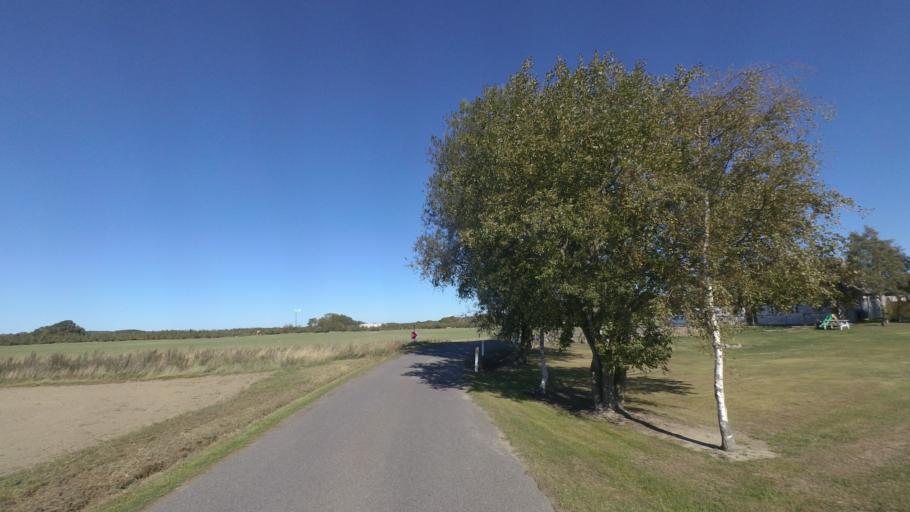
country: DK
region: Capital Region
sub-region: Bornholm Kommune
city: Nexo
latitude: 55.1206
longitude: 15.0484
